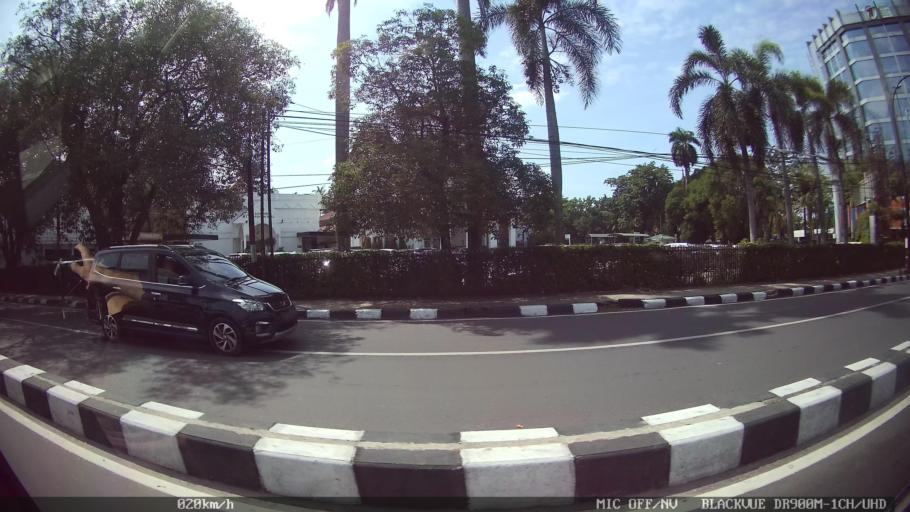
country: ID
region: North Sumatra
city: Medan
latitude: 3.5836
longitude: 98.6755
